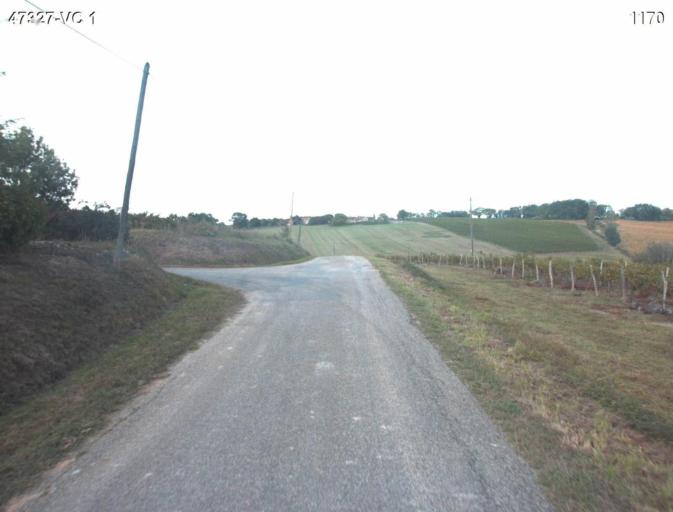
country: FR
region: Aquitaine
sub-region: Departement du Lot-et-Garonne
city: Barbaste
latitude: 44.1951
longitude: 0.2573
